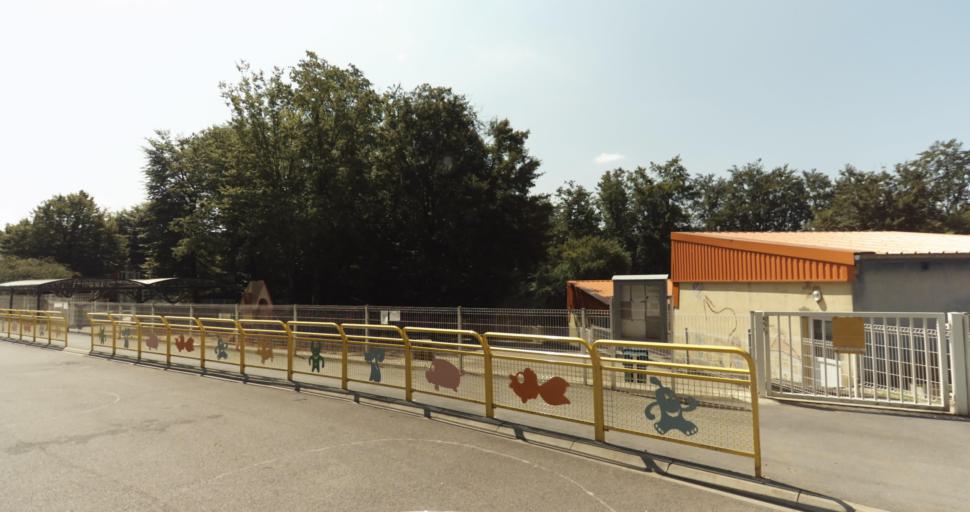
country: FR
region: Lorraine
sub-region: Departement de Meurthe-et-Moselle
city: Briey
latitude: 49.2592
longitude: 5.9269
